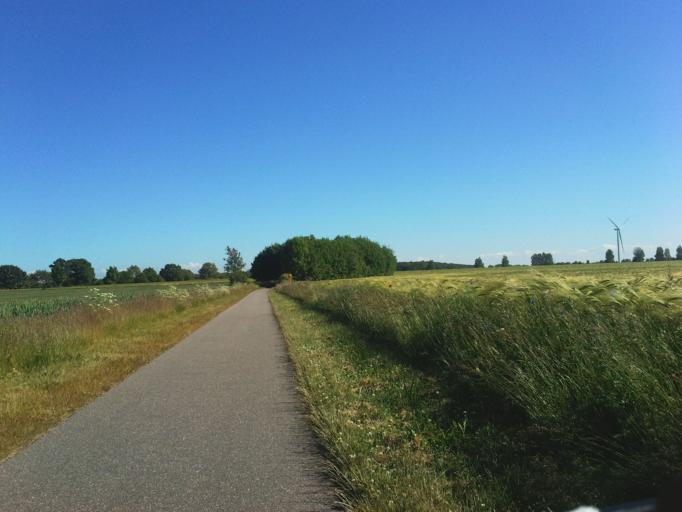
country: DE
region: Mecklenburg-Vorpommern
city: Nienhagen
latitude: 54.1500
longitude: 12.1874
